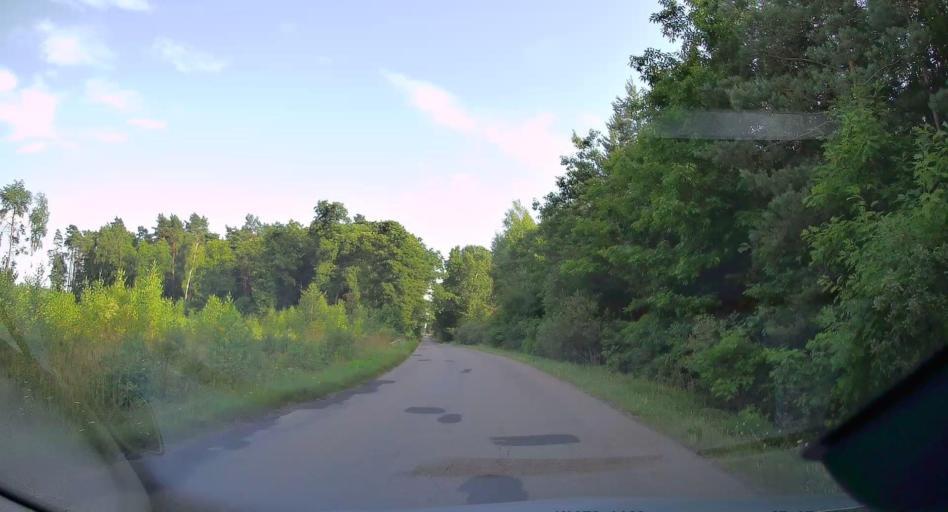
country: PL
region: Swietokrzyskie
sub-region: Powiat konecki
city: Konskie
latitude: 51.2278
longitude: 20.3837
